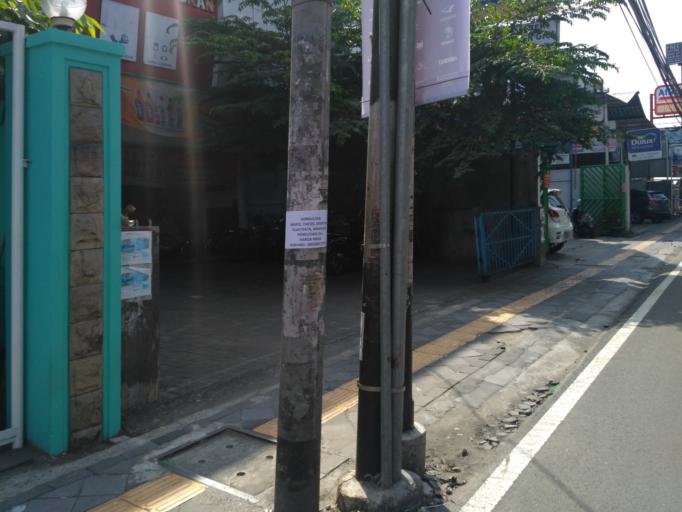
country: ID
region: Daerah Istimewa Yogyakarta
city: Depok
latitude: -7.7697
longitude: 110.4099
